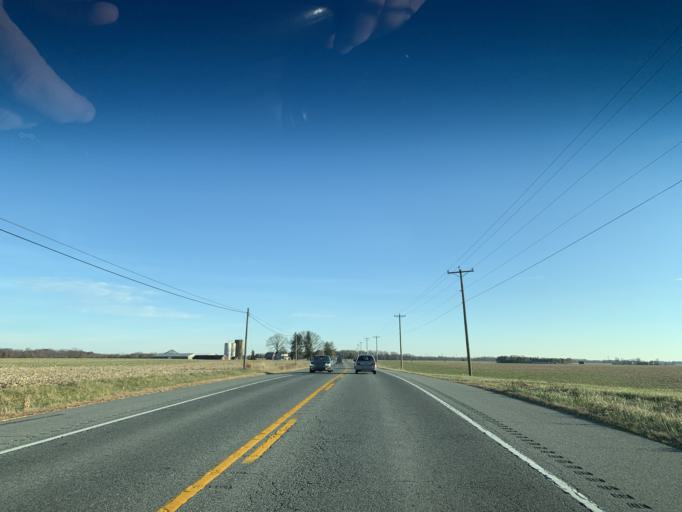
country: US
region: Delaware
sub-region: New Castle County
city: Middletown
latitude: 39.4427
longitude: -75.8659
